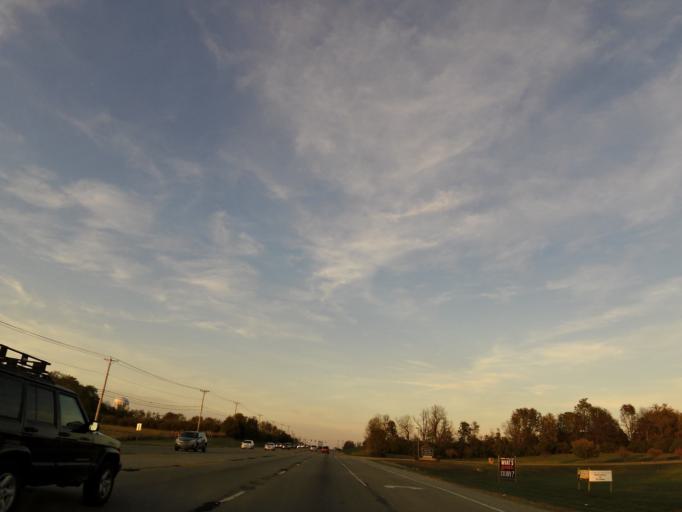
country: US
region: Kentucky
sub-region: Fayette County
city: Monticello
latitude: 37.9479
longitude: -84.5432
